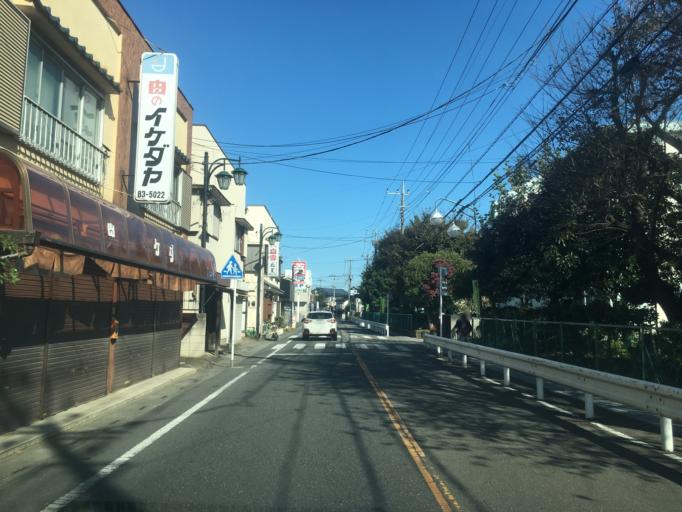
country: JP
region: Saitama
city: Sakado
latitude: 35.9609
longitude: 139.4069
